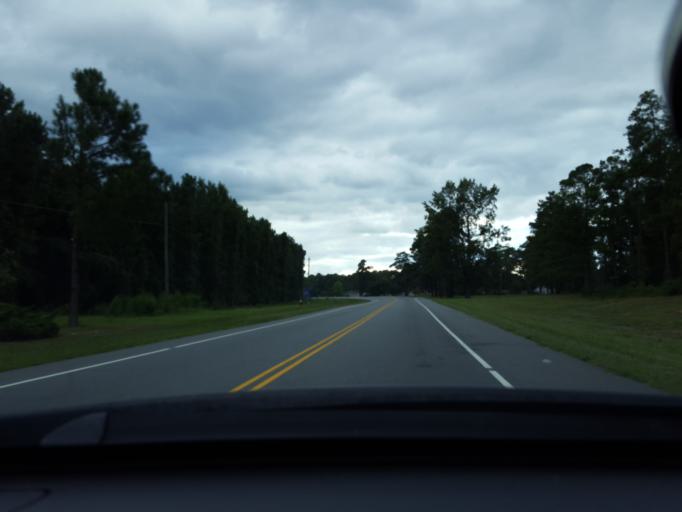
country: US
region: North Carolina
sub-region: Bladen County
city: Elizabethtown
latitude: 34.6550
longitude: -78.5145
